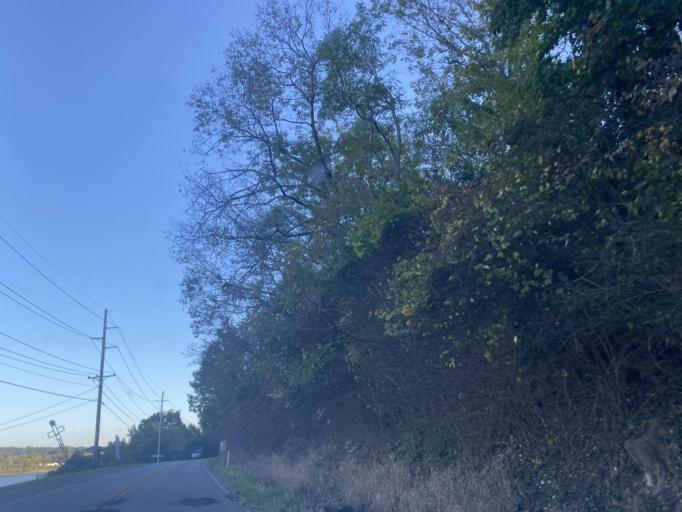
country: US
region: Kentucky
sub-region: Campbell County
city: Dayton
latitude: 39.1085
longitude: -84.4466
